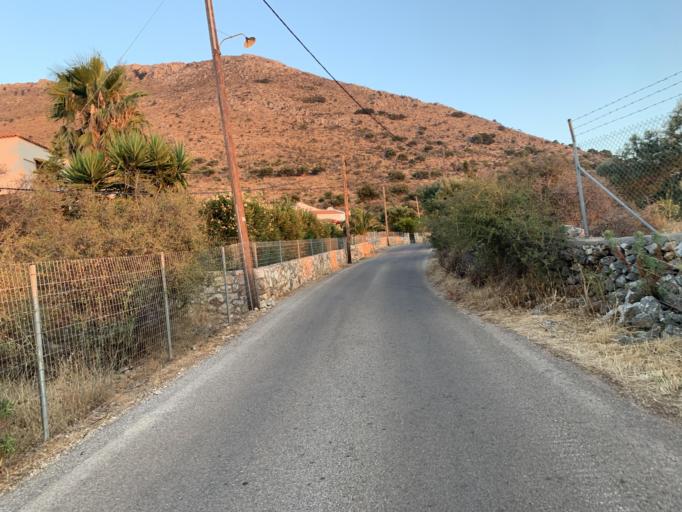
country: GR
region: Crete
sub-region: Nomos Chanias
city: Kalivai
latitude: 35.4505
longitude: 24.2274
